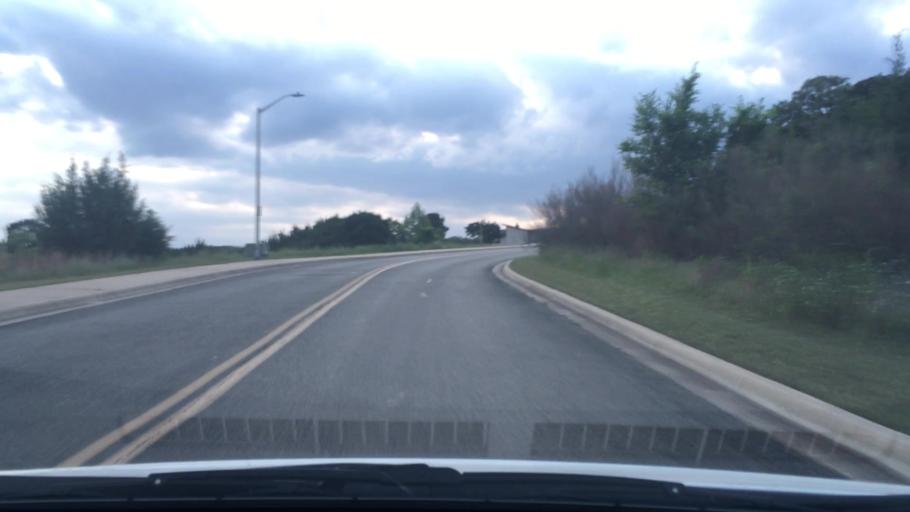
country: US
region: Texas
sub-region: Williamson County
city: Anderson Mill
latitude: 30.4511
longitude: -97.8557
